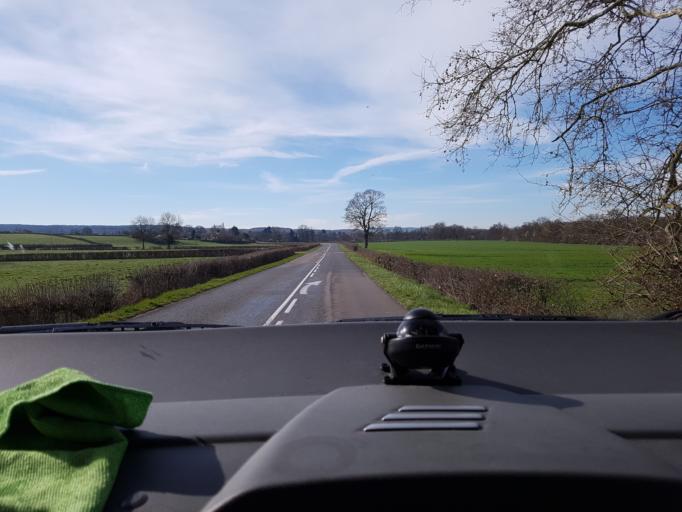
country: FR
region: Bourgogne
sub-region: Departement de Saone-et-Loire
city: Toulon-sur-Arroux
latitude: 46.7074
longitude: 4.1369
